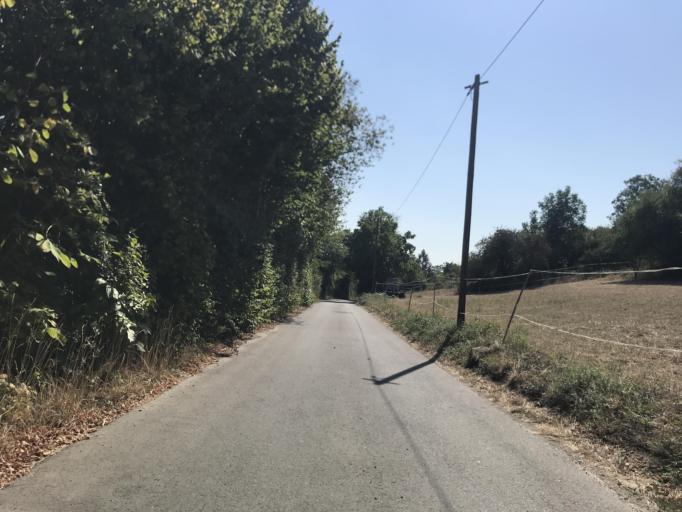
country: DE
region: Hesse
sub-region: Regierungsbezirk Darmstadt
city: Eltville
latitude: 50.0435
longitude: 8.1036
